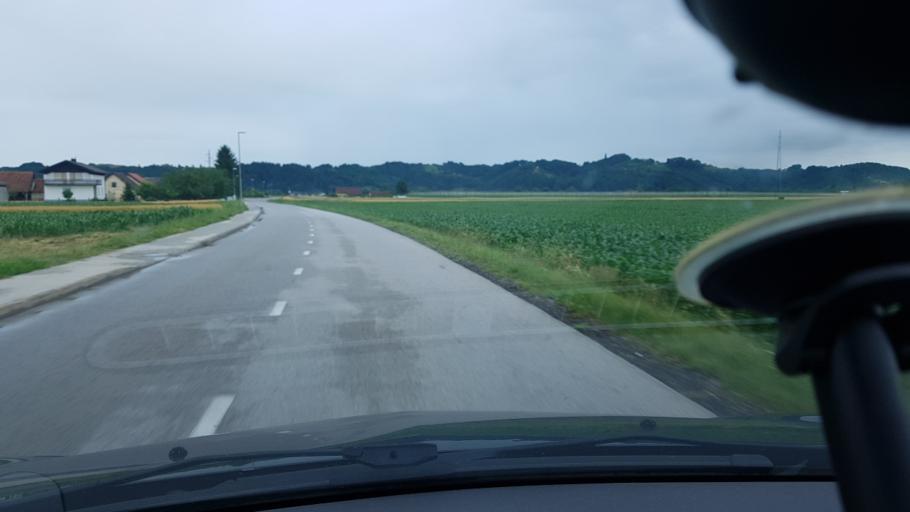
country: SI
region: Videm
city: Videm pri Ptuju
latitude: 46.3798
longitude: 15.8820
